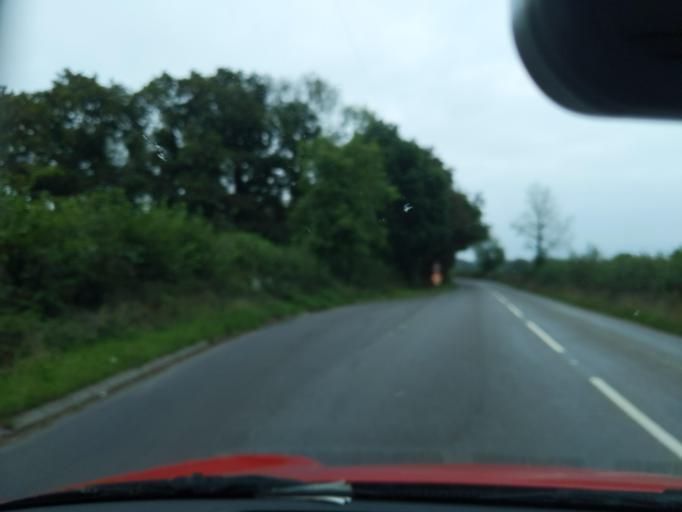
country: GB
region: England
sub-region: Devon
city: Okehampton
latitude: 50.8356
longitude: -4.0759
